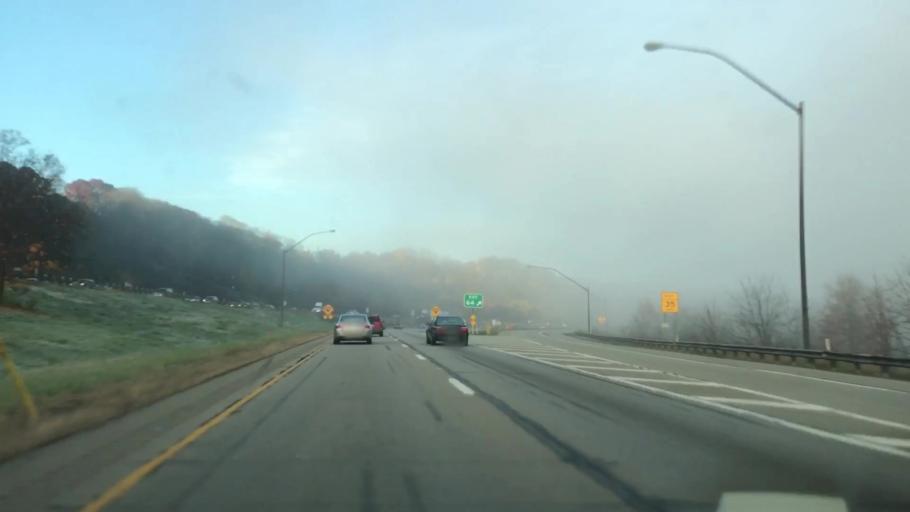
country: US
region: Pennsylvania
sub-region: Allegheny County
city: Emsworth
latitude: 40.5018
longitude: -80.1317
